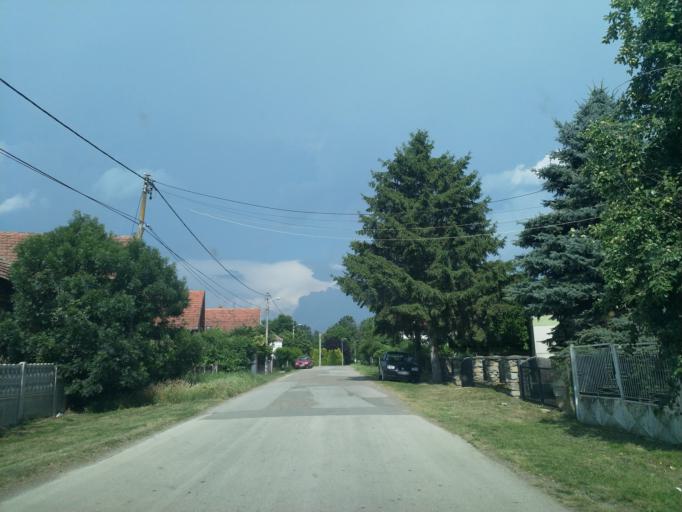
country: RS
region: Central Serbia
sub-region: Pomoravski Okrug
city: Cuprija
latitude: 43.9553
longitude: 21.3278
